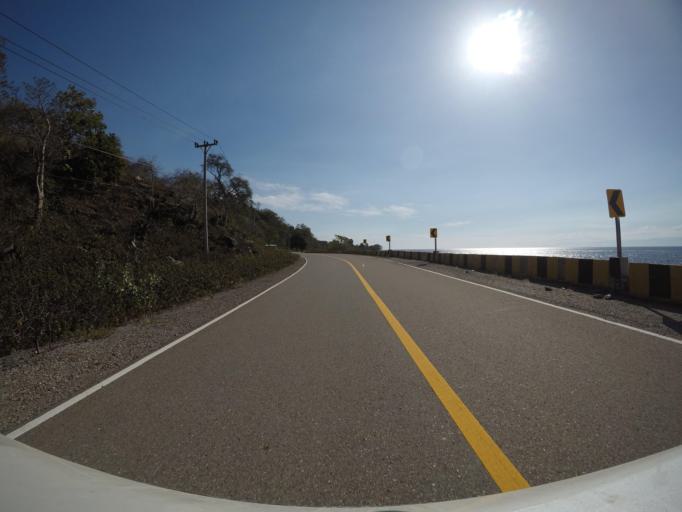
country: TL
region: Liquica
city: Maubara
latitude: -8.6177
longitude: 125.1798
